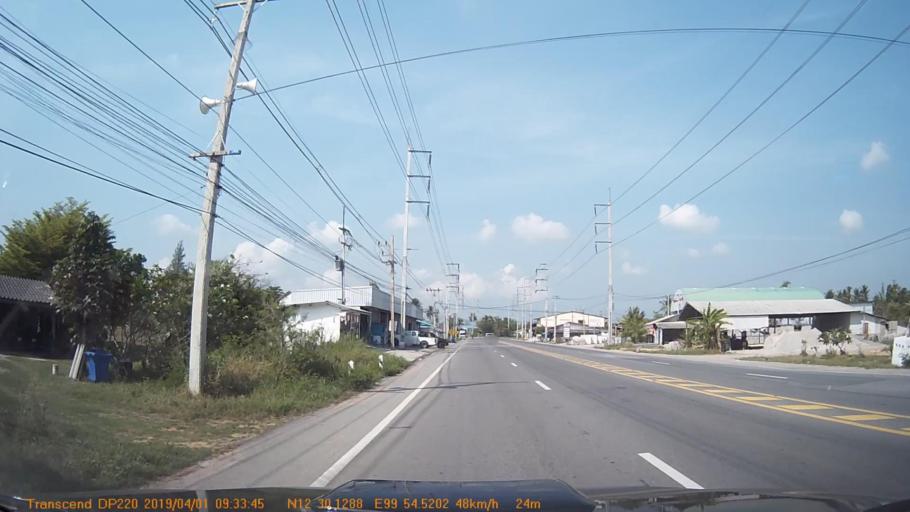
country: TH
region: Prachuap Khiri Khan
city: Hua Hin
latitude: 12.5021
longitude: 99.9086
